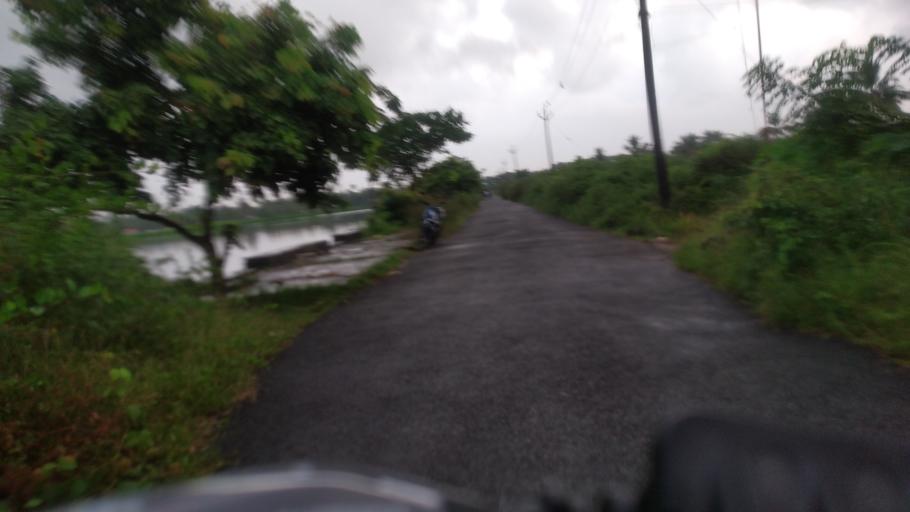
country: IN
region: Kerala
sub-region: Ernakulam
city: Elur
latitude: 10.0157
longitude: 76.2192
